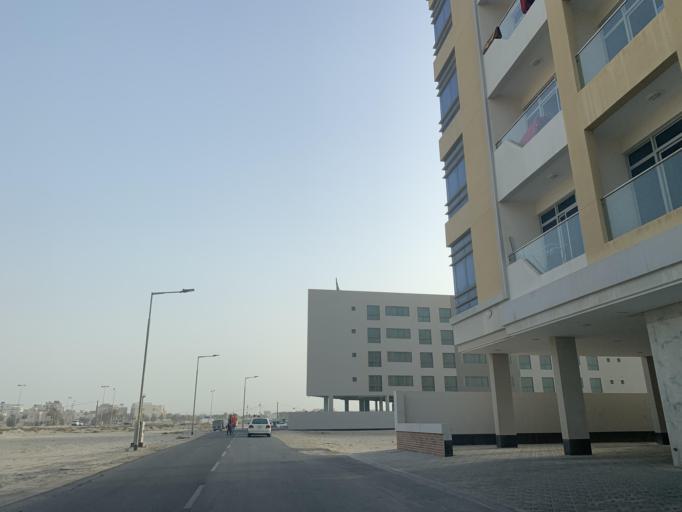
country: BH
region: Manama
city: Jidd Hafs
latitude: 26.2391
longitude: 50.5261
